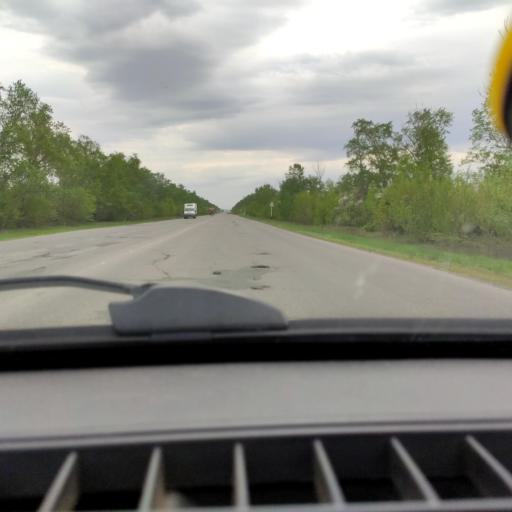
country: RU
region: Samara
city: Tol'yatti
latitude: 53.6077
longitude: 49.4110
